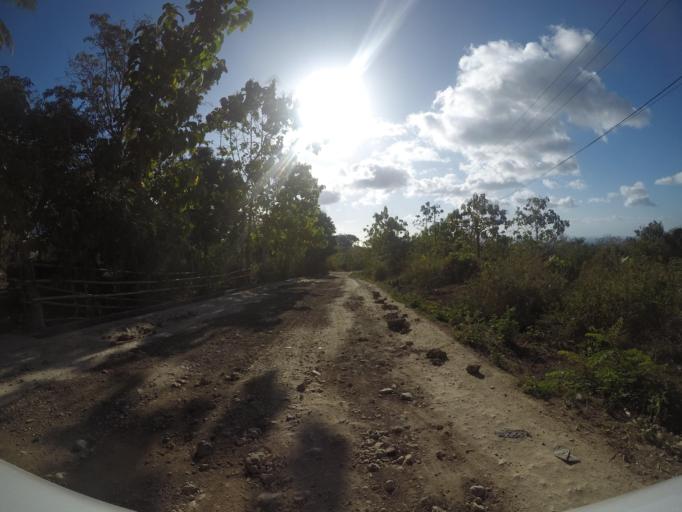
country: TL
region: Lautem
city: Lospalos
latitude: -8.4434
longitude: 126.8659
